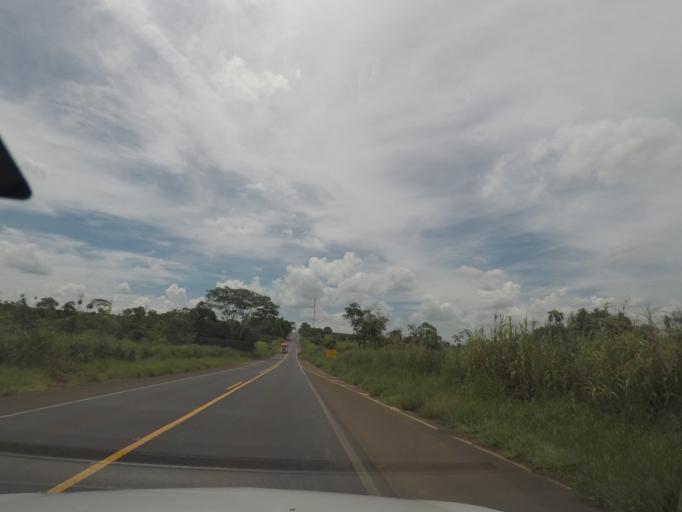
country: BR
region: Sao Paulo
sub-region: Barretos
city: Barretos
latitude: -20.4277
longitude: -48.6285
